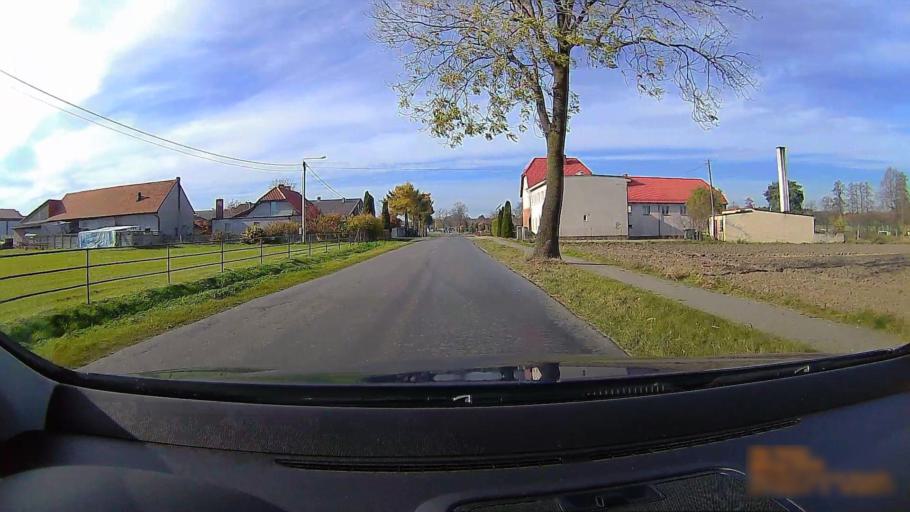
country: PL
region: Greater Poland Voivodeship
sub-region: Powiat ostrzeszowski
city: Doruchow
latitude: 51.4295
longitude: 18.0390
